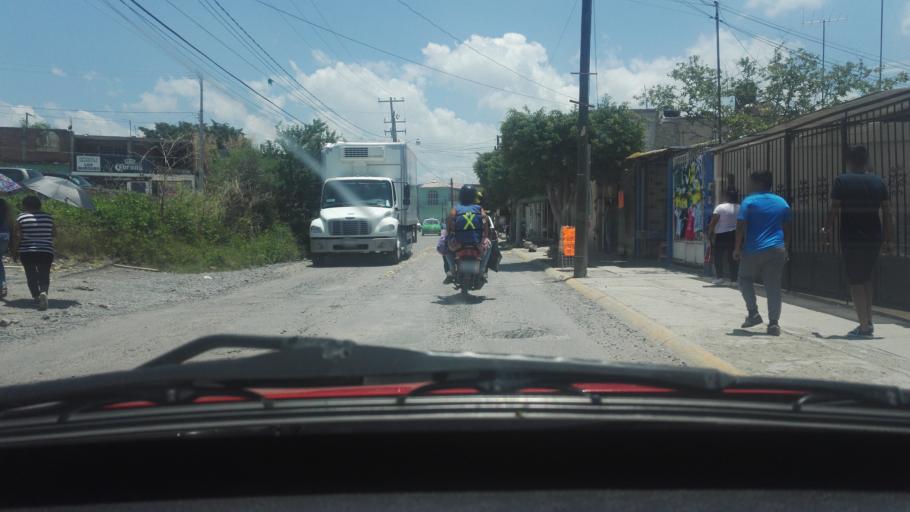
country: MX
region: Guanajuato
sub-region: Leon
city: San Jose de Duran (Los Troncoso)
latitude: 21.0835
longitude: -101.6316
